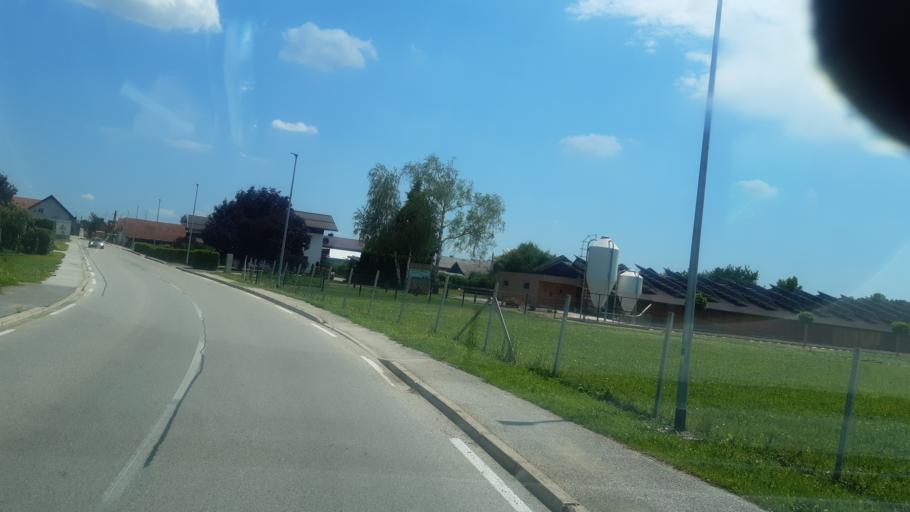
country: SI
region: Moravske Toplice
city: Moravske Toplice
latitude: 46.6700
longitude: 16.2175
